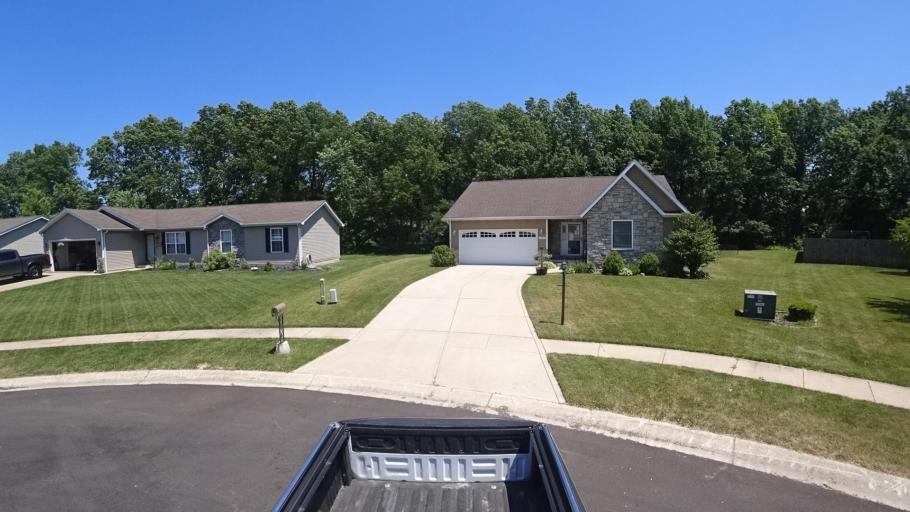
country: US
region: Indiana
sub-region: Porter County
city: Burns Harbor
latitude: 41.6016
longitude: -87.1351
